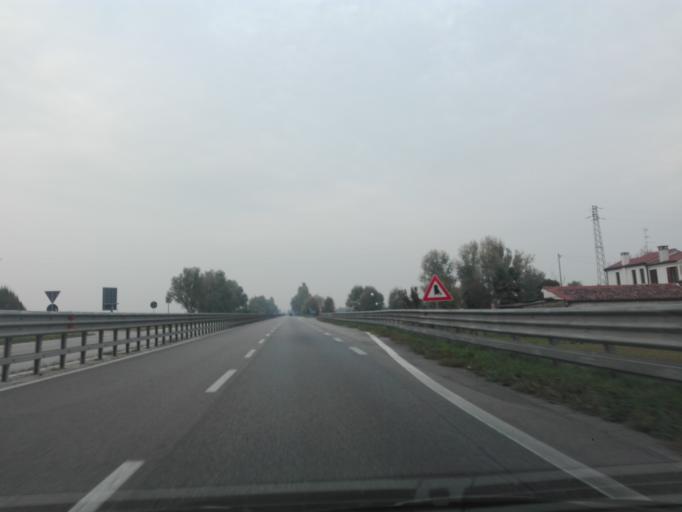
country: IT
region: Veneto
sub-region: Provincia di Rovigo
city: San Bellino
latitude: 45.0250
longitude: 11.5892
